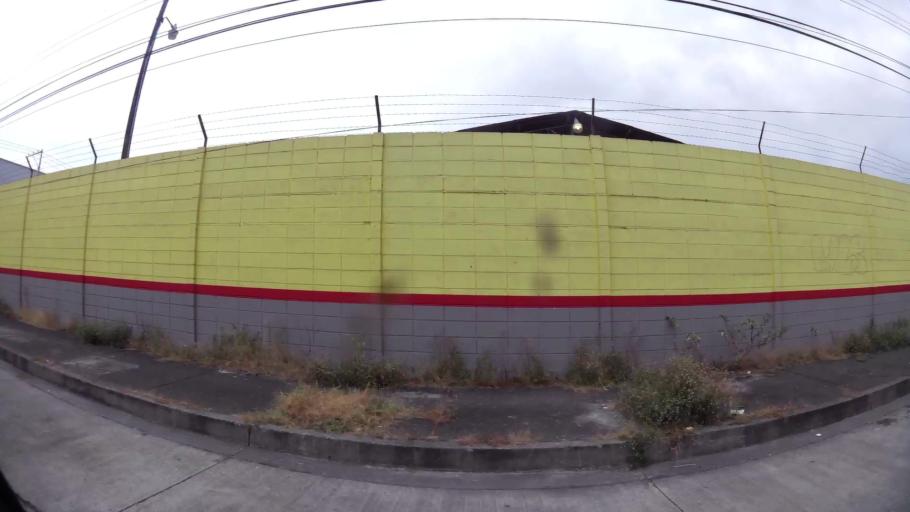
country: EC
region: Guayas
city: Eloy Alfaro
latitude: -2.1438
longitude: -79.8857
